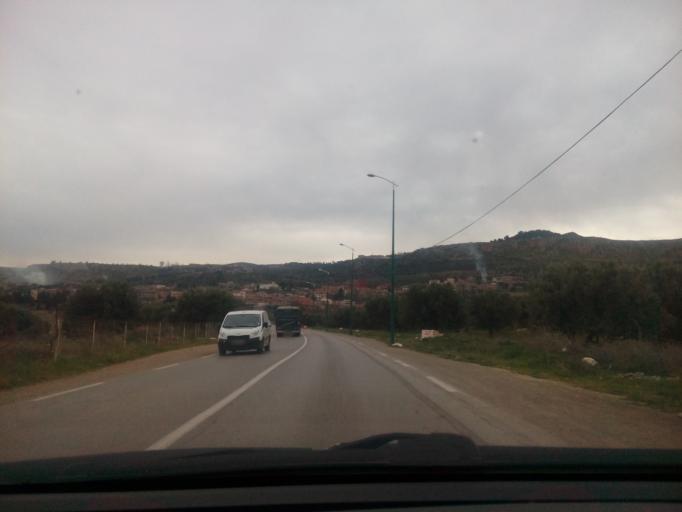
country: DZ
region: Tlemcen
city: Mansoura
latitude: 34.8652
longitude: -1.3471
